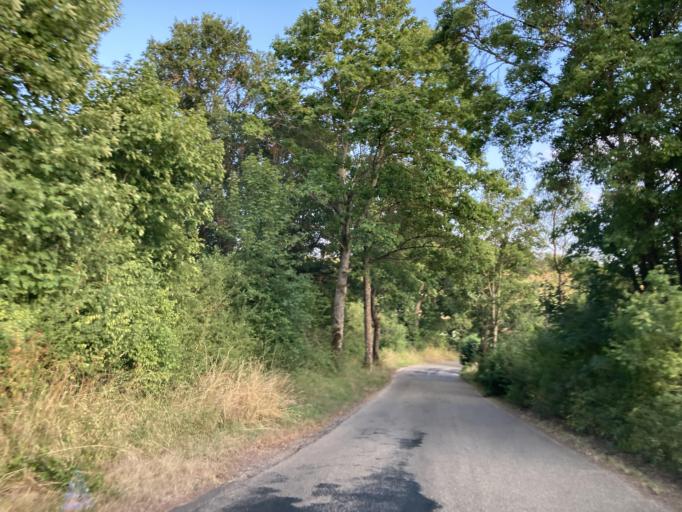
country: DE
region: Baden-Wuerttemberg
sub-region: Karlsruhe Region
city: Ebhausen
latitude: 48.5950
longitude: 8.6812
